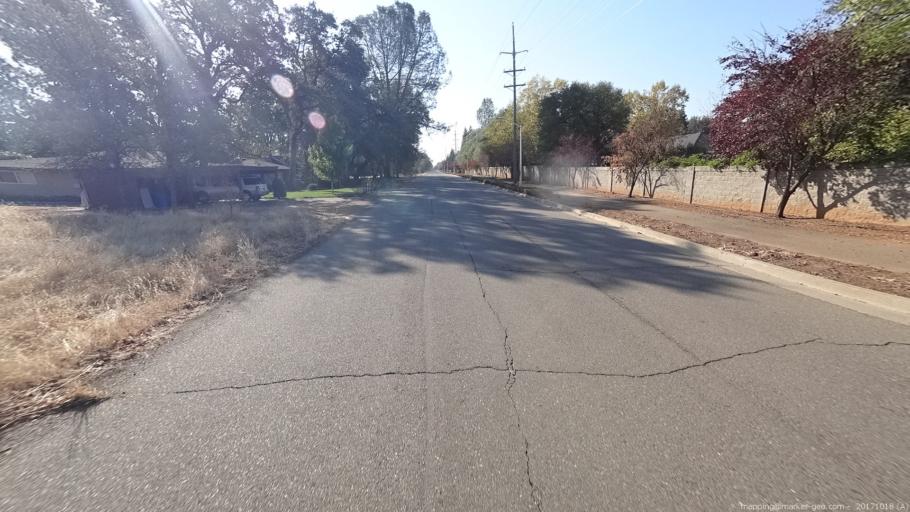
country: US
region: California
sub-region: Shasta County
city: Palo Cedro
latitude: 40.5444
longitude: -122.3147
